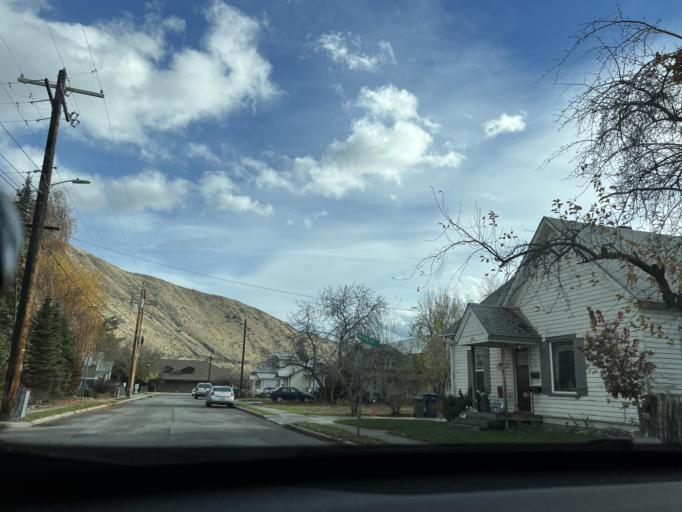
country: US
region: Washington
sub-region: Chelan County
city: Cashmere
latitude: 47.5236
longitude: -120.4693
